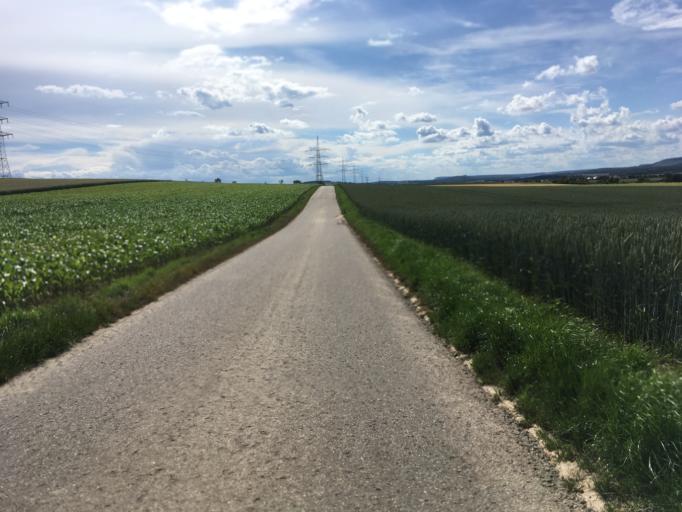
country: DE
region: Baden-Wuerttemberg
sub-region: Regierungsbezirk Stuttgart
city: Vaihingen an der Enz
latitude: 48.9407
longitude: 8.9922
